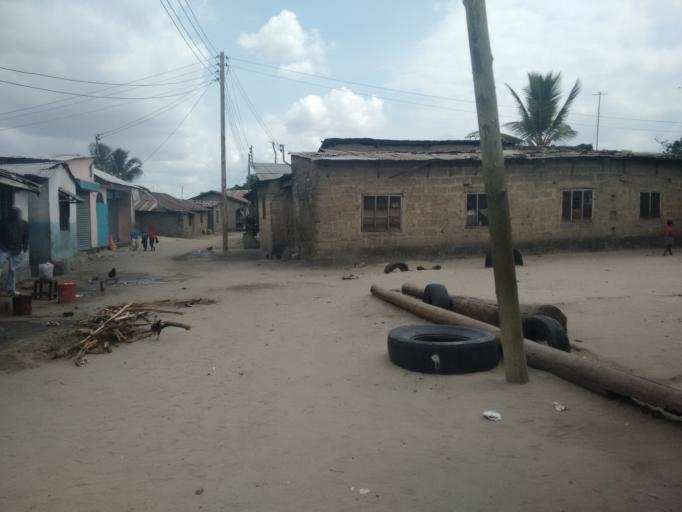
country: TZ
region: Dar es Salaam
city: Dar es Salaam
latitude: -6.8571
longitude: 39.2535
